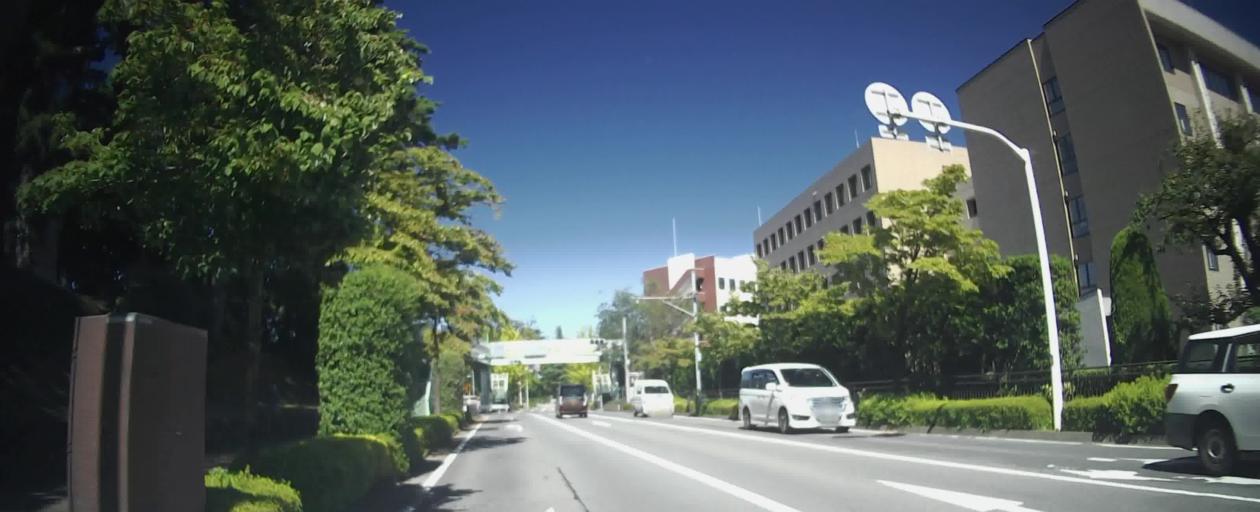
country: JP
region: Gunma
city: Maebashi-shi
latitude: 36.3919
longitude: 139.0618
